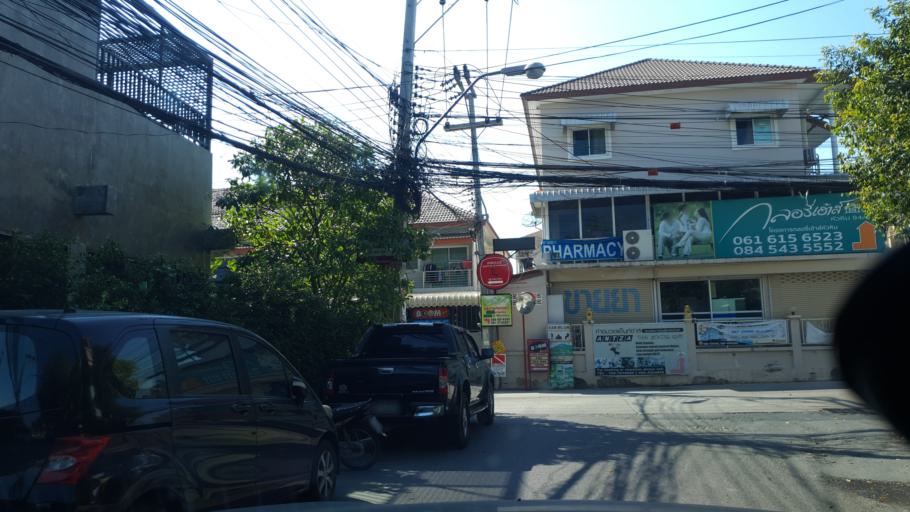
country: TH
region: Prachuap Khiri Khan
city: Hua Hin
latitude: 12.5548
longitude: 99.9528
